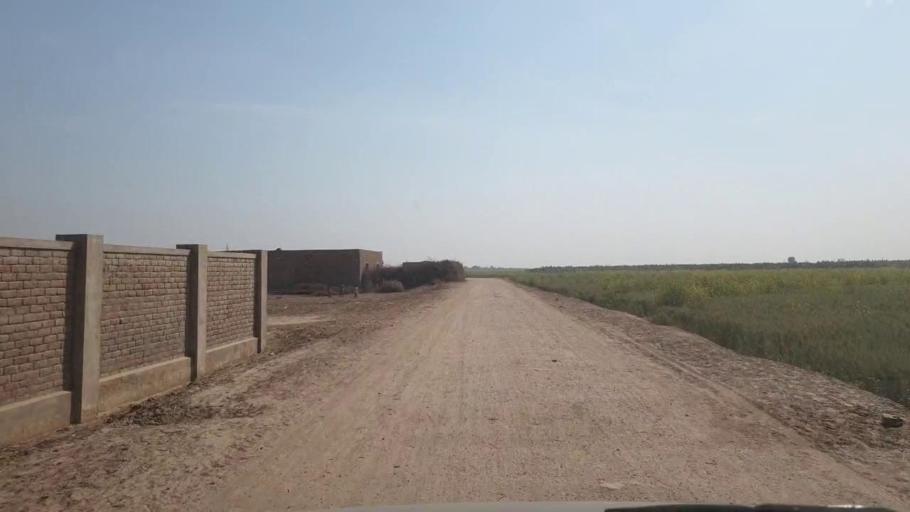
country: PK
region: Sindh
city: Chambar
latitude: 25.3746
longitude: 68.8082
